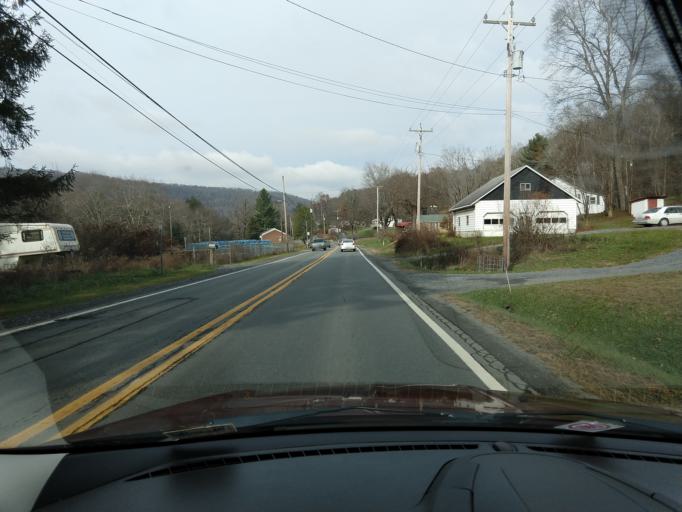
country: US
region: West Virginia
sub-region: Greenbrier County
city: Rainelle
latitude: 37.9844
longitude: -80.7208
